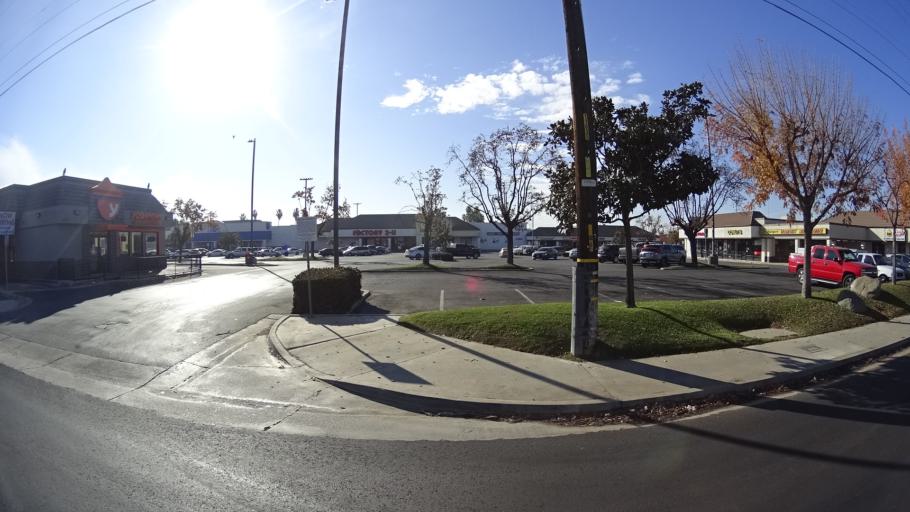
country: US
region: California
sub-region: Kern County
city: Greenfield
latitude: 35.3176
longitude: -119.0205
